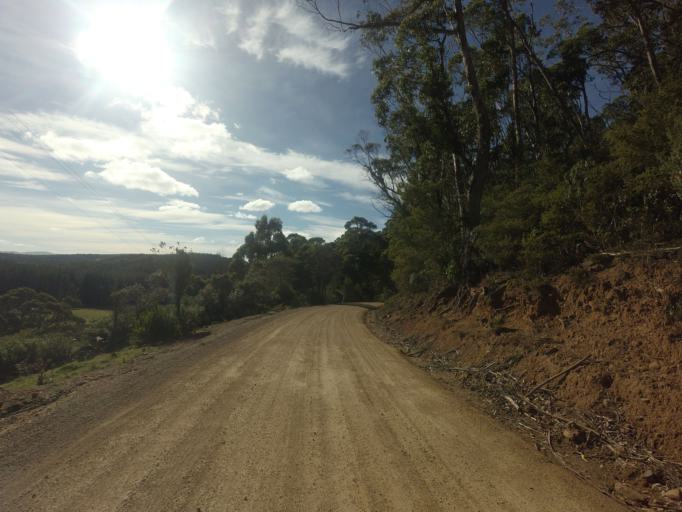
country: AU
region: Tasmania
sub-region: Clarence
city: Sandford
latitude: -43.1839
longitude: 147.7711
